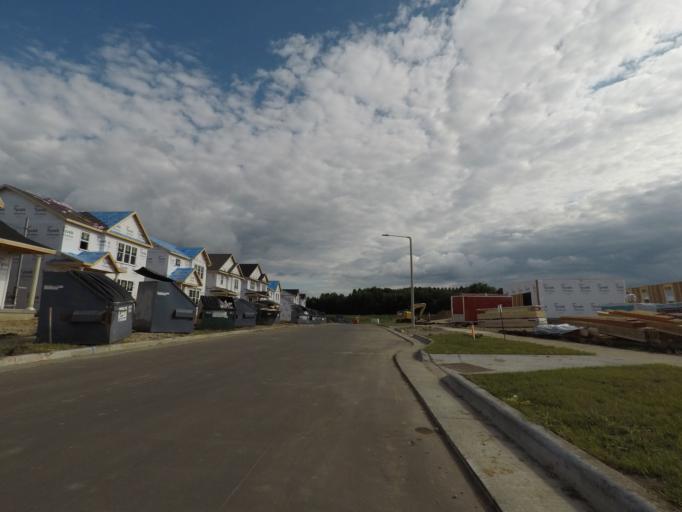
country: US
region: Wisconsin
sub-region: Dane County
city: Verona
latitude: 43.0501
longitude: -89.5499
